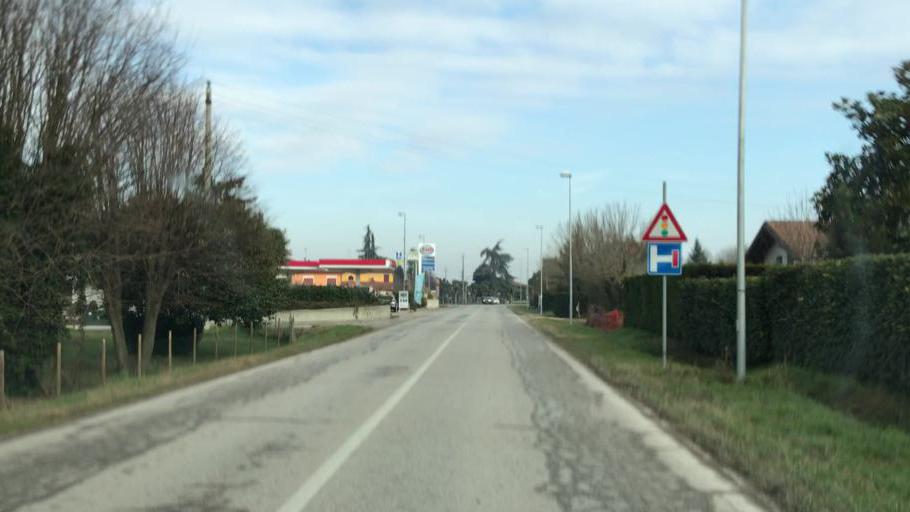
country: IT
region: Veneto
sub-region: Provincia di Rovigo
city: Fratta Polesine
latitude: 45.0280
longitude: 11.6478
